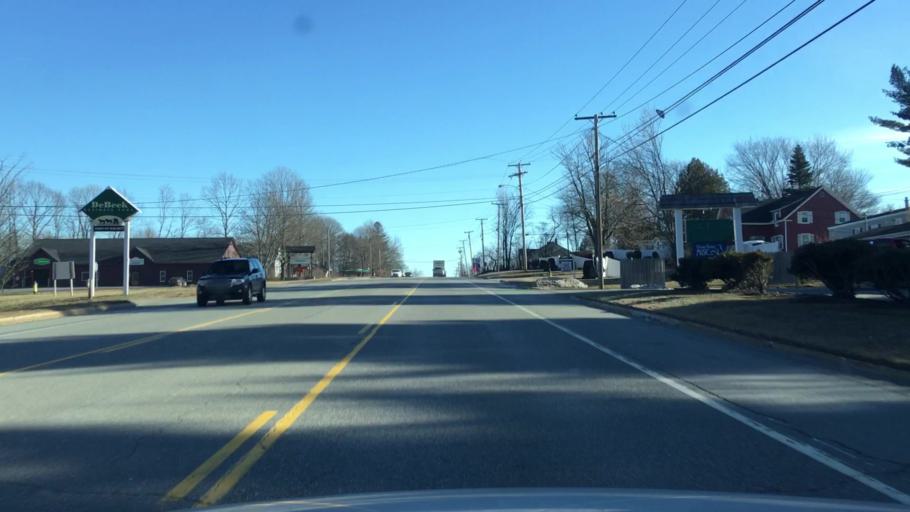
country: US
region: Maine
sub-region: Penobscot County
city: Holden
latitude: 44.7660
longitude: -68.7090
